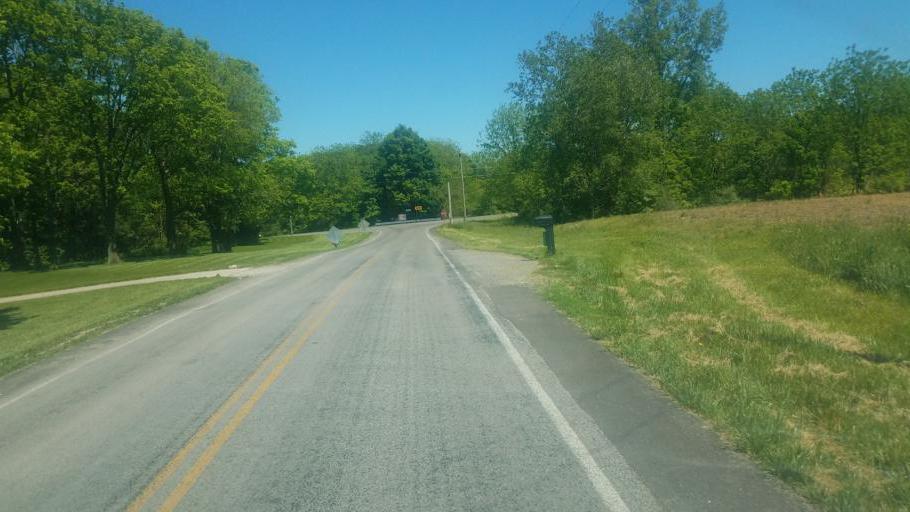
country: US
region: Ohio
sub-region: Champaign County
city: Saint Paris
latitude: 40.1746
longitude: -83.9568
